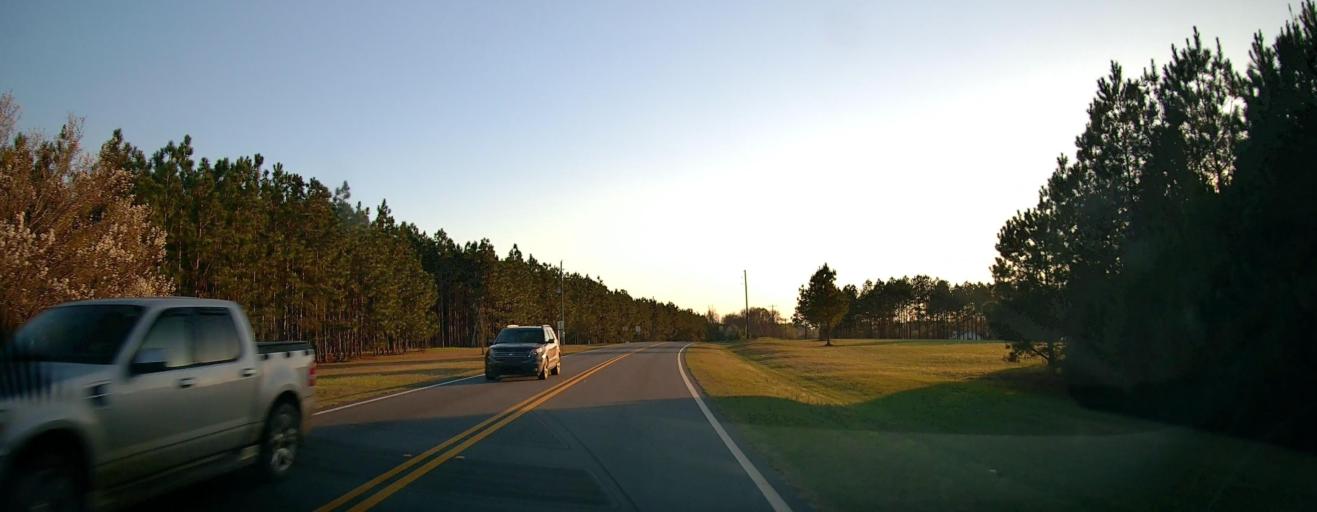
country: US
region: Georgia
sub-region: Dodge County
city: Chester
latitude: 32.3749
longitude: -82.9956
